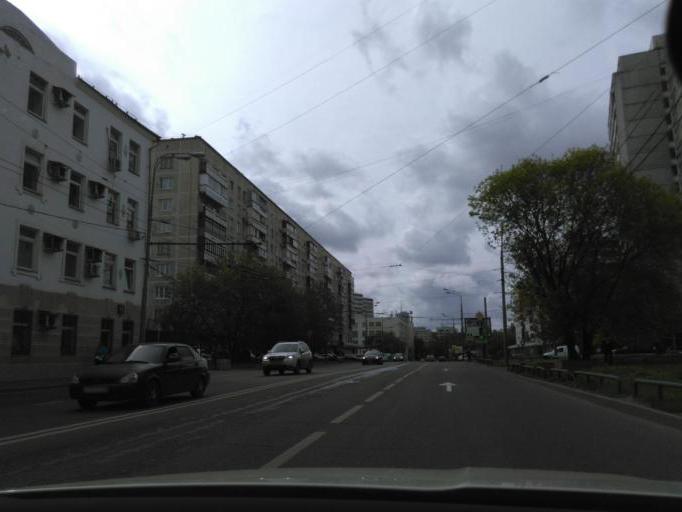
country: RU
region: Moscow
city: Mar'ina Roshcha
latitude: 55.7843
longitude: 37.6416
